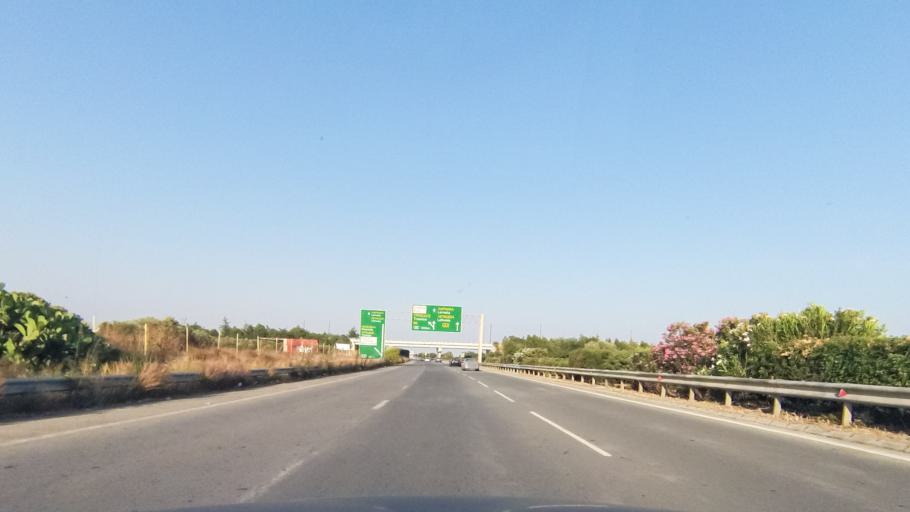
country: CY
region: Limassol
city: Pano Polemidia
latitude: 34.6873
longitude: 32.9951
